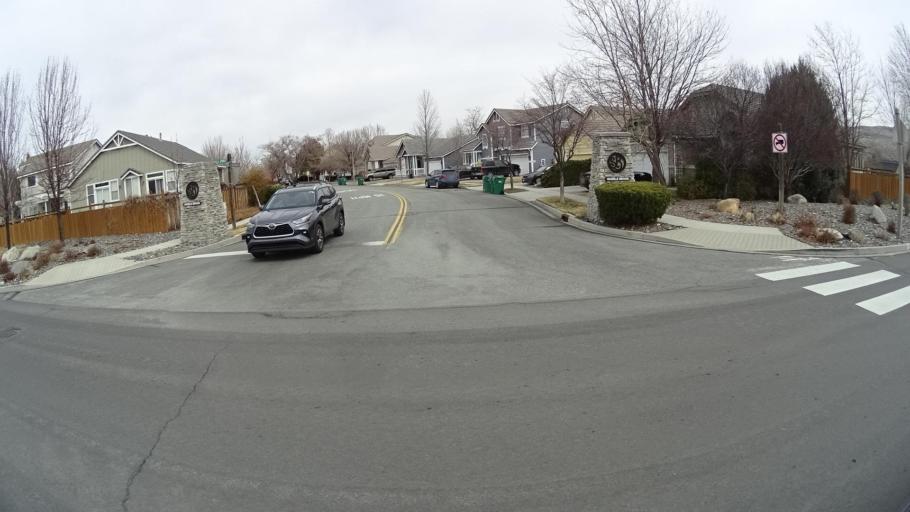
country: US
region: Nevada
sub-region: Washoe County
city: Spanish Springs
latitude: 39.6216
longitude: -119.6825
